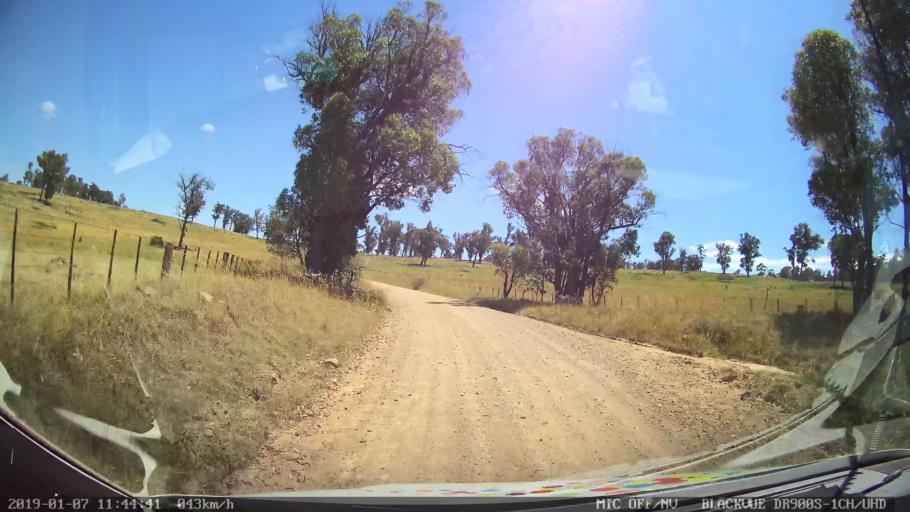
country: AU
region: New South Wales
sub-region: Guyra
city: Guyra
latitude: -30.3510
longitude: 151.6065
